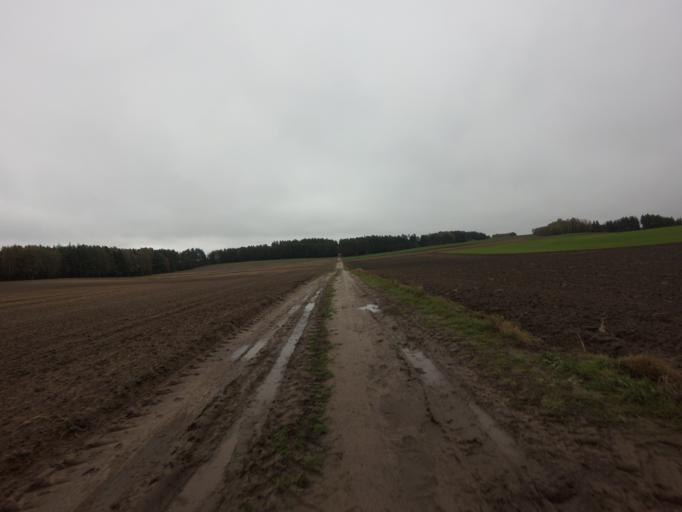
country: PL
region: Pomeranian Voivodeship
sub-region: Powiat kartuski
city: Stezyca
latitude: 54.1694
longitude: 17.9353
